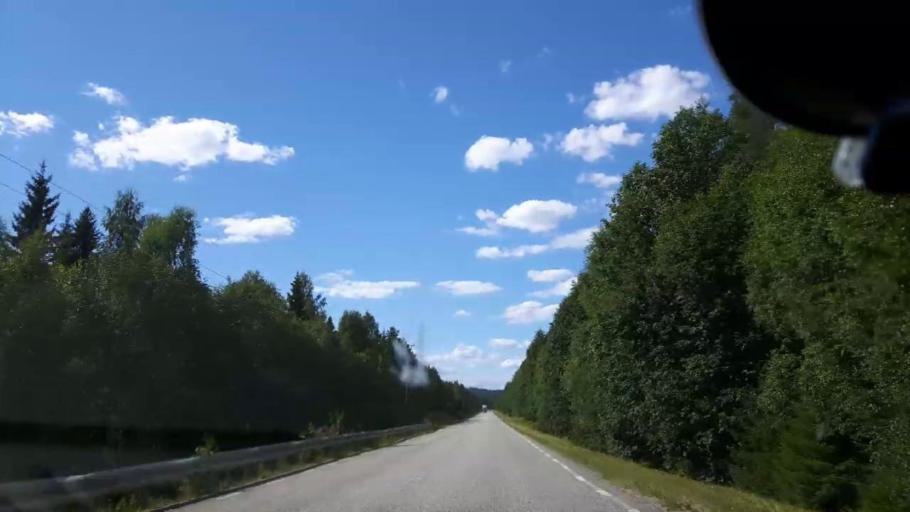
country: SE
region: Vaesternorrland
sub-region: Ange Kommun
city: Fransta
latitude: 62.7609
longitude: 16.2744
